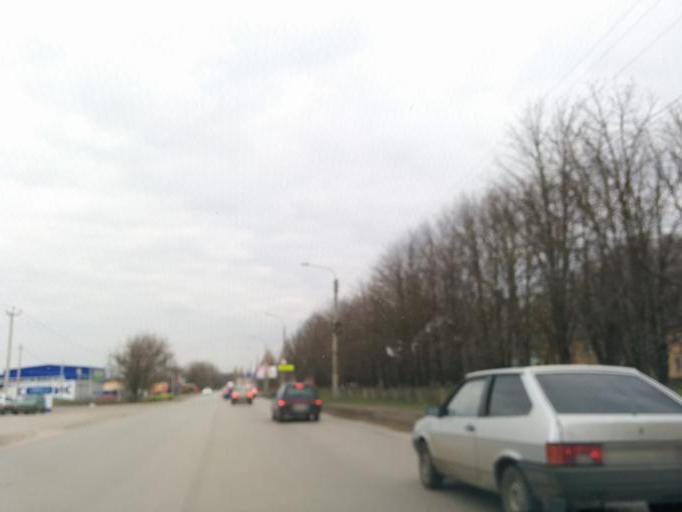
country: RU
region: Rostov
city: Novocherkassk
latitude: 47.4837
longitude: 40.1029
